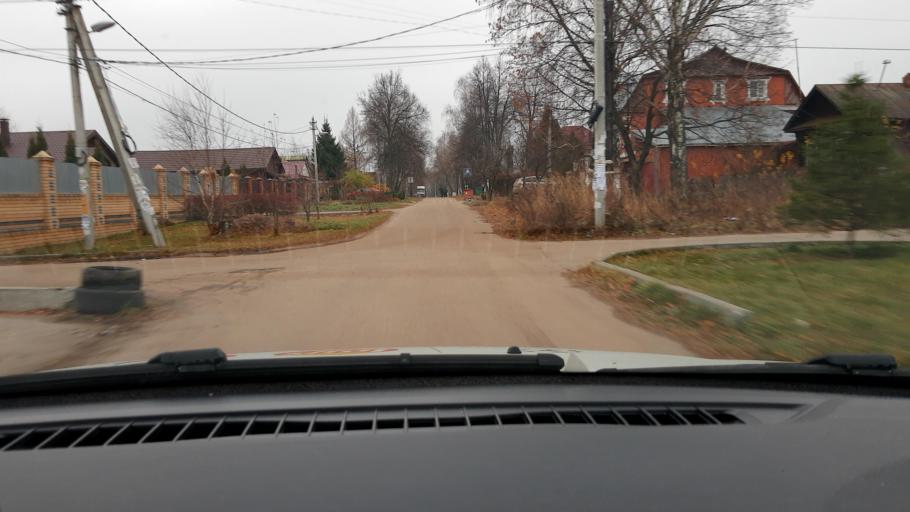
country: RU
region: Nizjnij Novgorod
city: Gorbatovka
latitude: 56.2051
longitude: 43.7659
